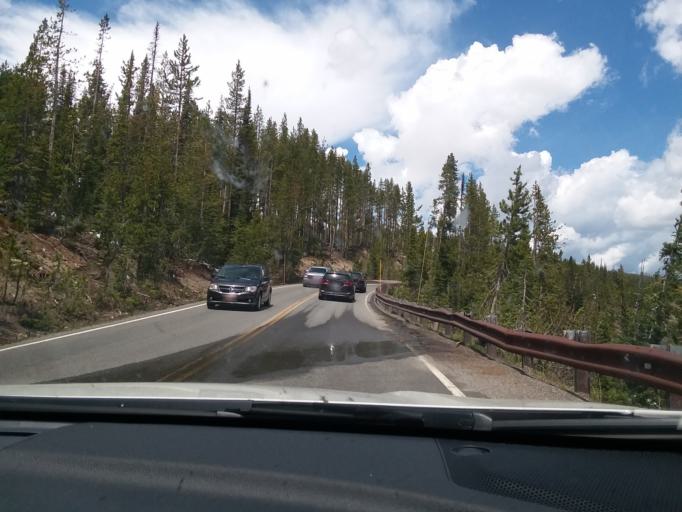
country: US
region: Montana
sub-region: Gallatin County
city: West Yellowstone
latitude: 44.2042
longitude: -110.6604
